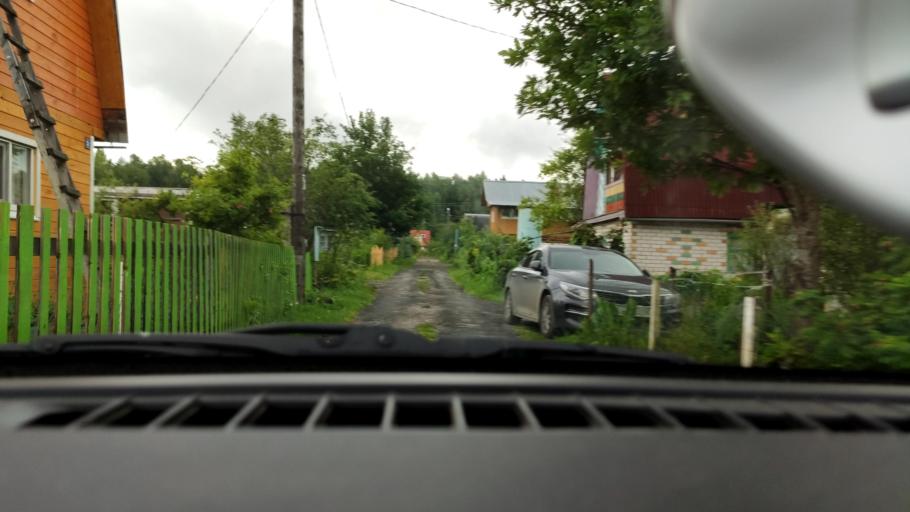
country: RU
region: Perm
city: Overyata
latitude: 58.0543
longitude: 55.9769
